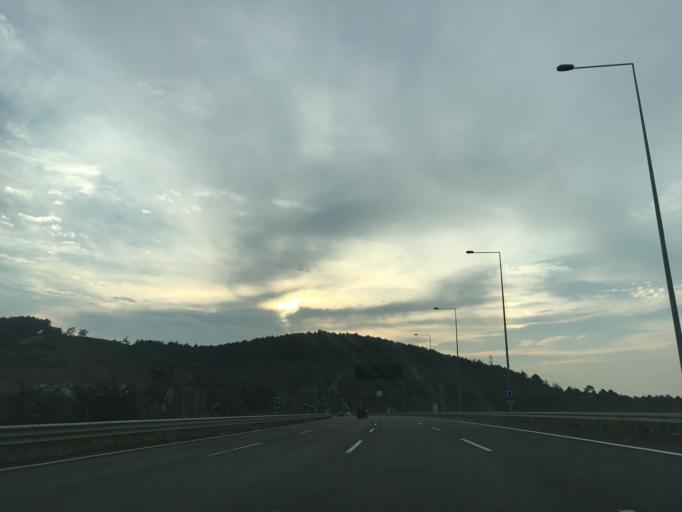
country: TR
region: Istanbul
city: Samandira
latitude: 41.0561
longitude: 29.1851
